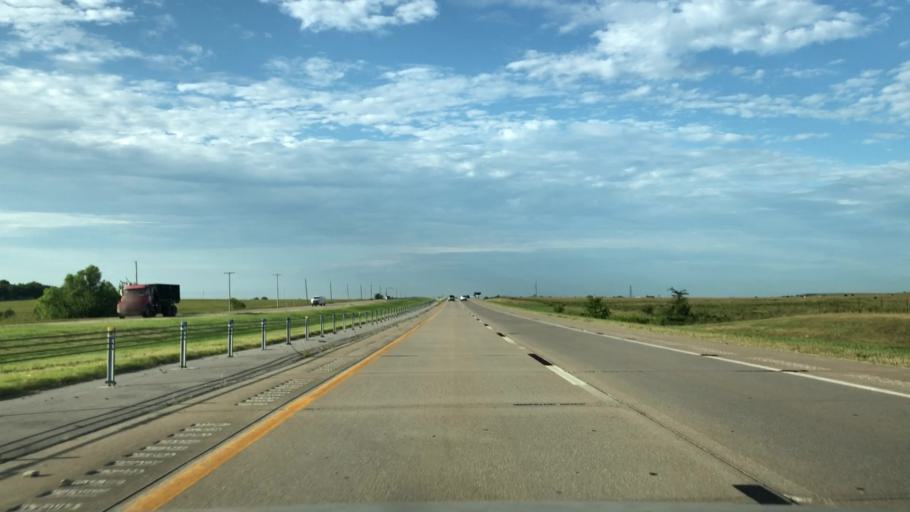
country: US
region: Oklahoma
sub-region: Osage County
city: Skiatook
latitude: 36.3859
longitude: -95.9205
